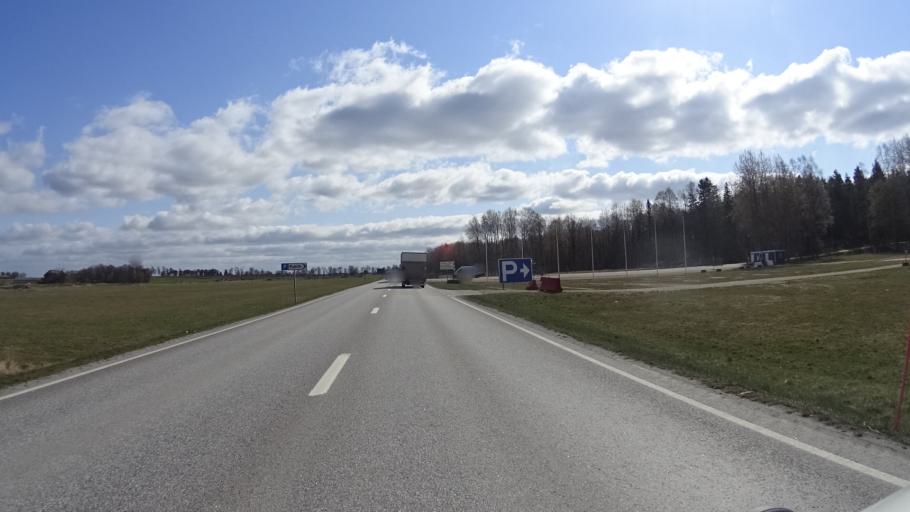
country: SE
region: OEstergoetland
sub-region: Mjolby Kommun
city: Mantorp
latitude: 58.3753
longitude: 15.2818
